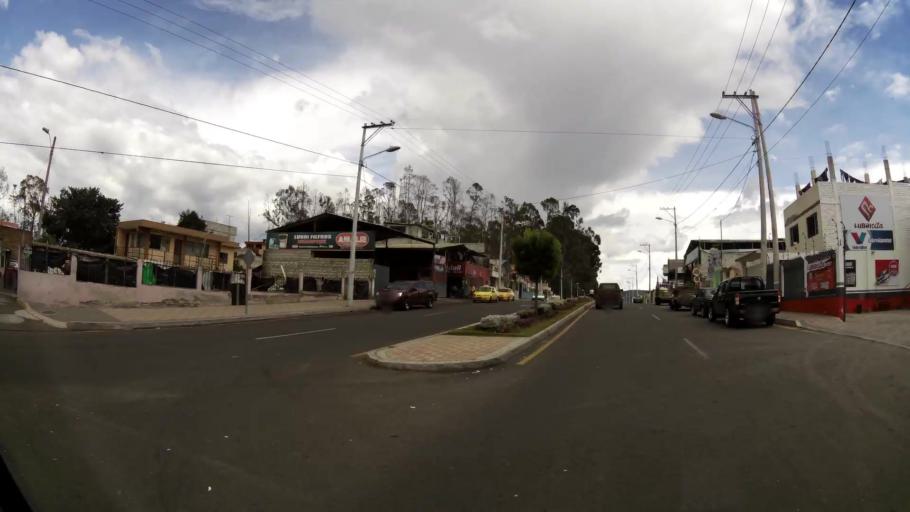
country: EC
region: Tungurahua
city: Ambato
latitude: -1.2608
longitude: -78.6109
